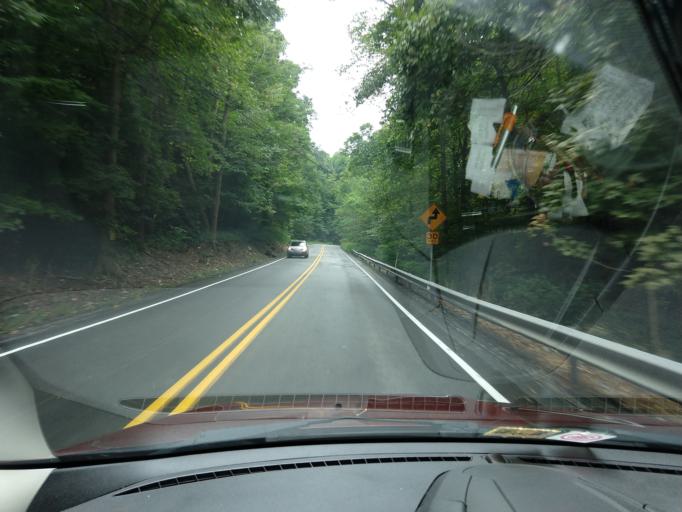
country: US
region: Pennsylvania
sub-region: Washington County
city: Baidland
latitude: 40.1701
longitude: -79.9958
